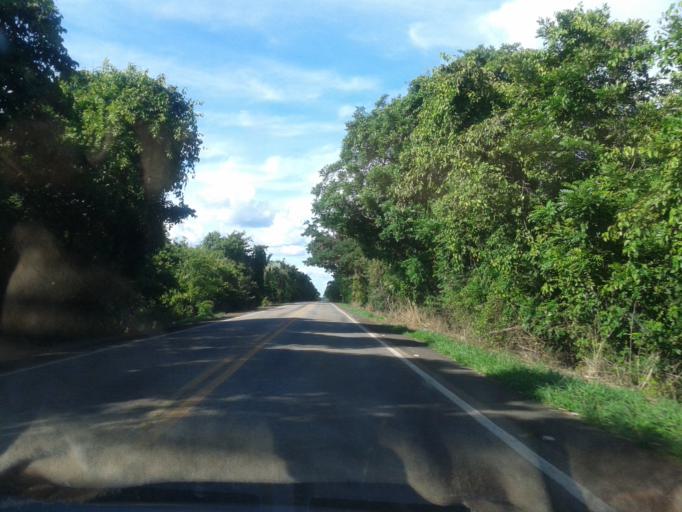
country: BR
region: Goias
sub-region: Mozarlandia
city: Mozarlandia
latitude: -14.5996
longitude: -50.5112
